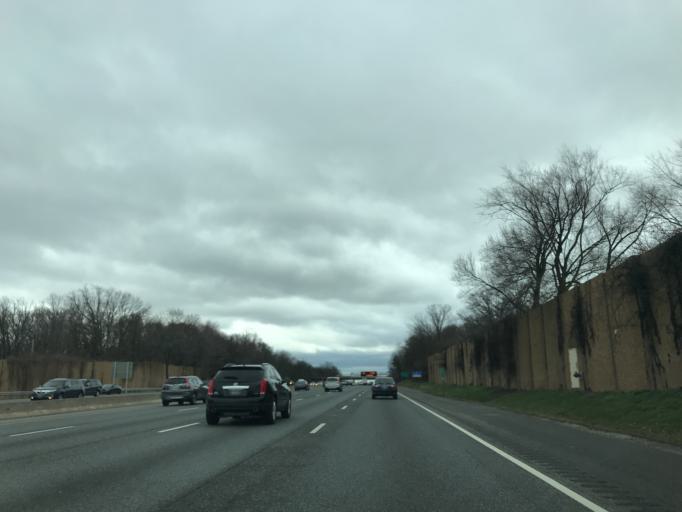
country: US
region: Maryland
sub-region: Baltimore County
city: Woodlawn
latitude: 39.3372
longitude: -76.7449
